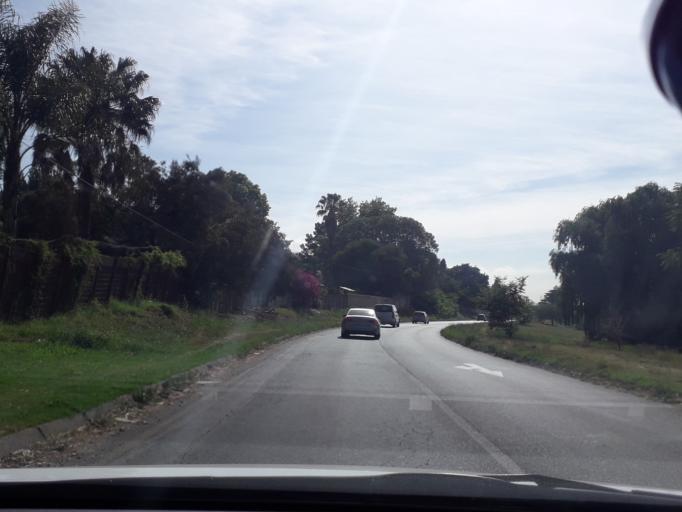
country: ZA
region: Gauteng
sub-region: City of Johannesburg Metropolitan Municipality
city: Roodepoort
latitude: -26.1194
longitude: 27.9257
